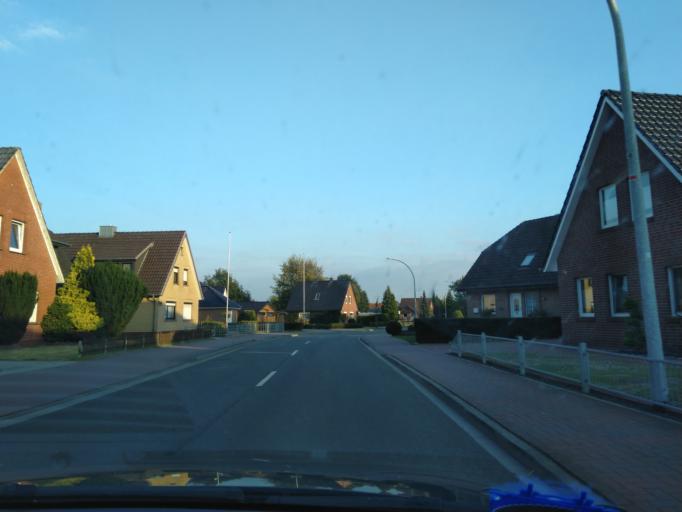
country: DE
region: Lower Saxony
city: Papenburg
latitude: 53.0702
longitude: 7.4240
